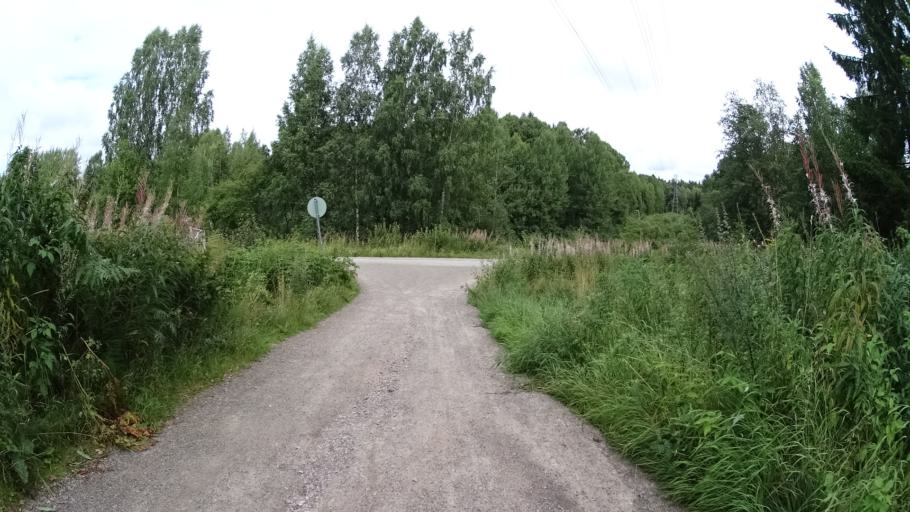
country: FI
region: Uusimaa
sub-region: Helsinki
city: Teekkarikylae
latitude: 60.2680
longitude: 24.8929
